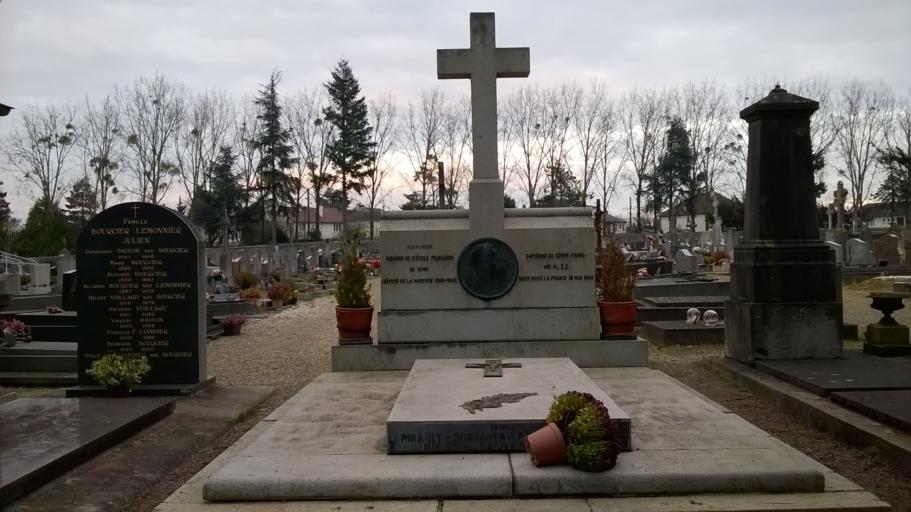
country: FR
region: Pays de la Loire
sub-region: Departement de la Mayenne
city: Laval
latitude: 48.0720
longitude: -0.7537
